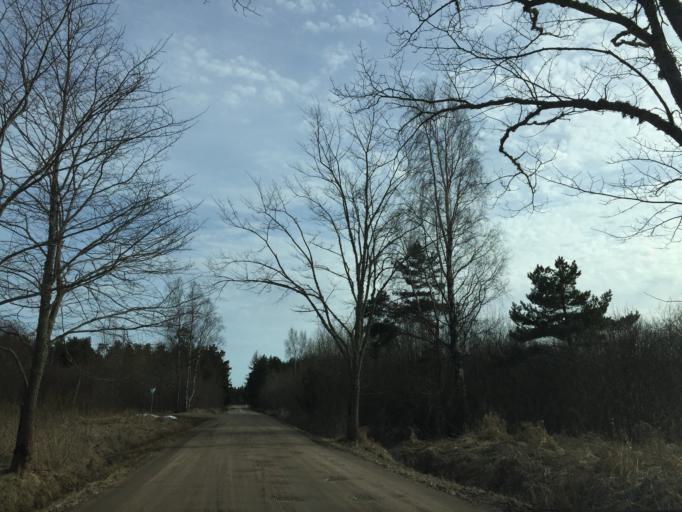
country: EE
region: Paernumaa
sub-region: Paernu linn
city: Parnu
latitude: 58.2420
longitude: 24.4828
